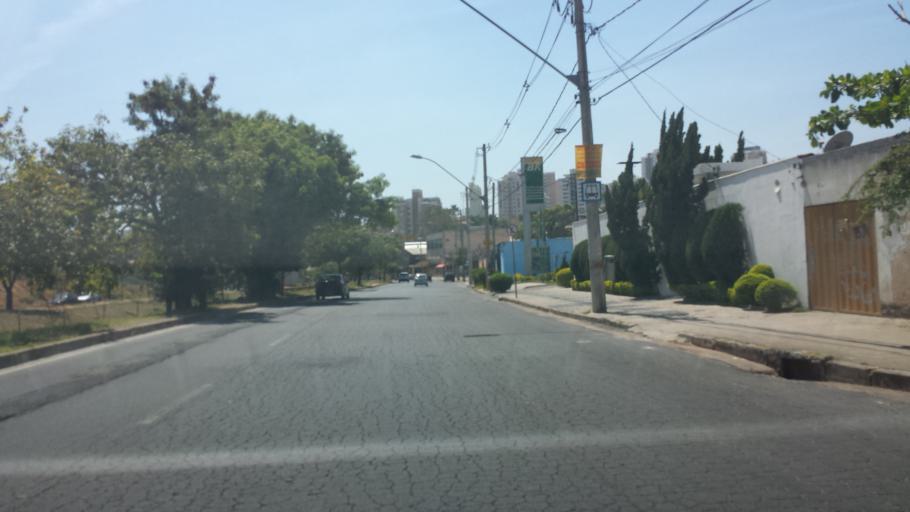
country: BR
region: Minas Gerais
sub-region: Belo Horizonte
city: Belo Horizonte
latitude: -19.8781
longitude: -43.9924
